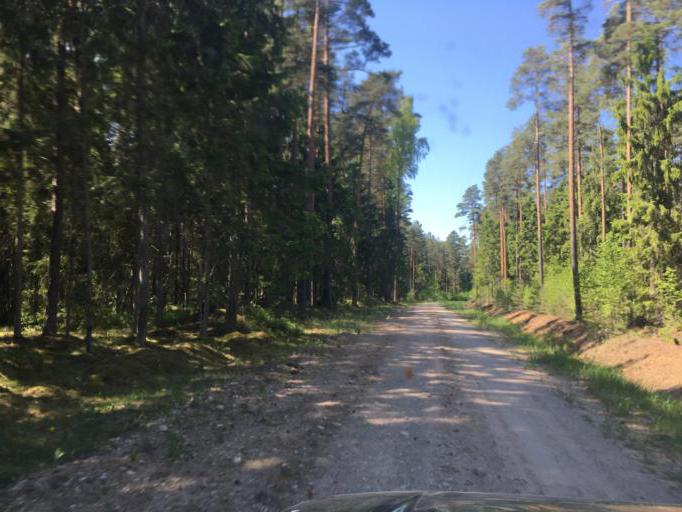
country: LV
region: Talsu Rajons
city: Valdemarpils
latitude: 57.4405
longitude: 22.6709
